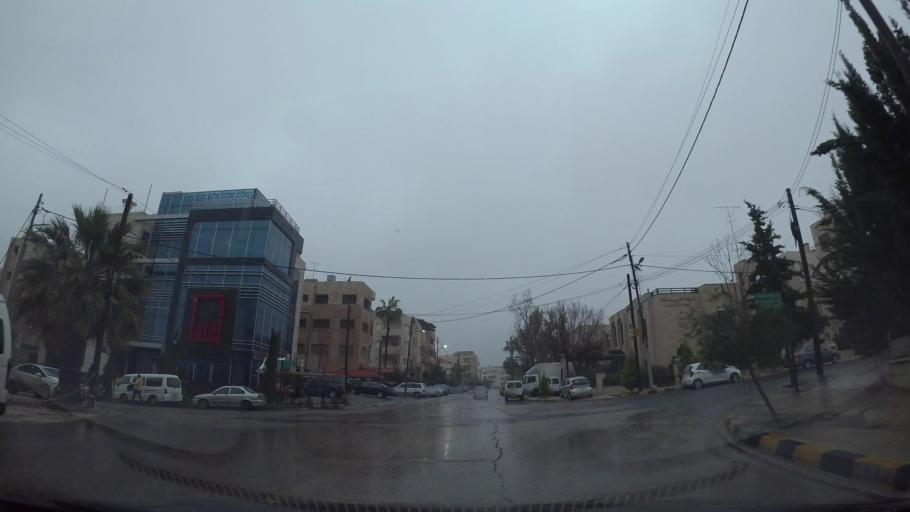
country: JO
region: Amman
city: Wadi as Sir
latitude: 31.9699
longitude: 35.8708
